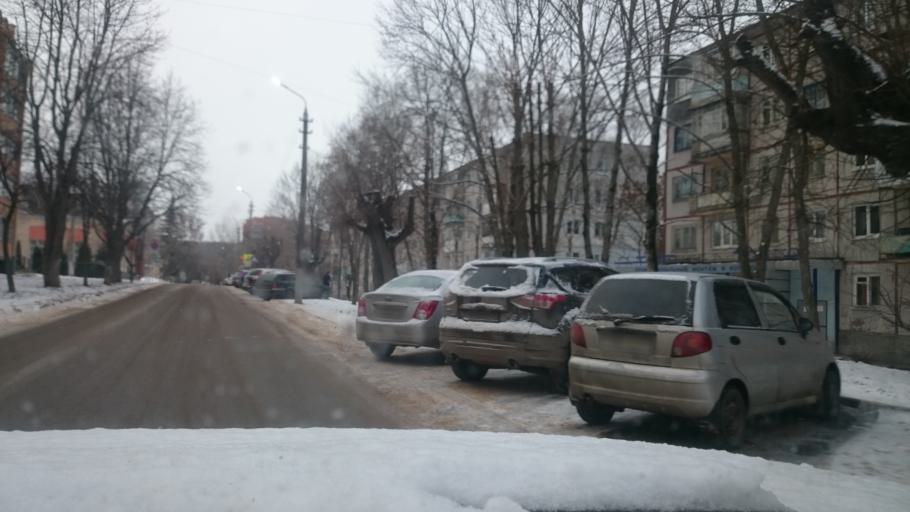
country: RU
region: Tula
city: Tula
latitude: 54.1877
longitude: 37.6013
